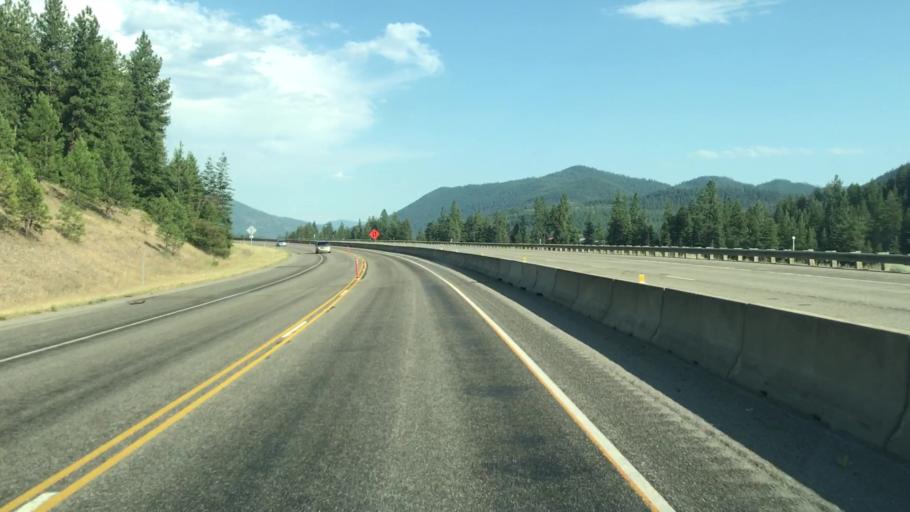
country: US
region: Montana
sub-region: Mineral County
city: Superior
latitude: 47.2185
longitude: -114.9573
